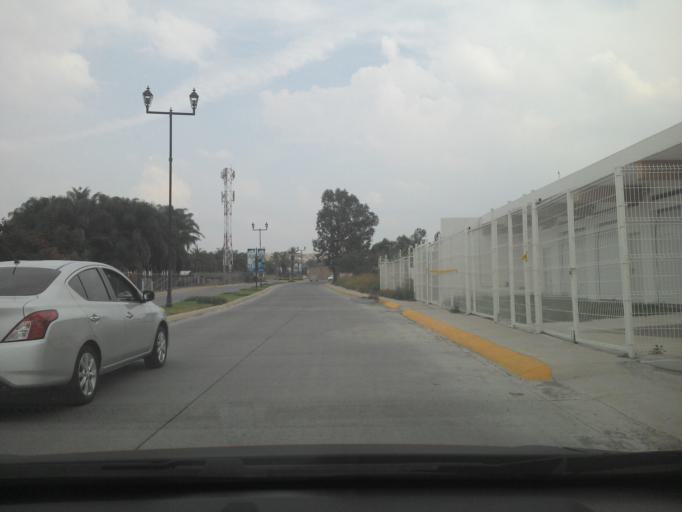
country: MX
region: Jalisco
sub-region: Tlajomulco de Zuniga
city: Lomas de San Agustin
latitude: 20.5299
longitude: -103.4681
